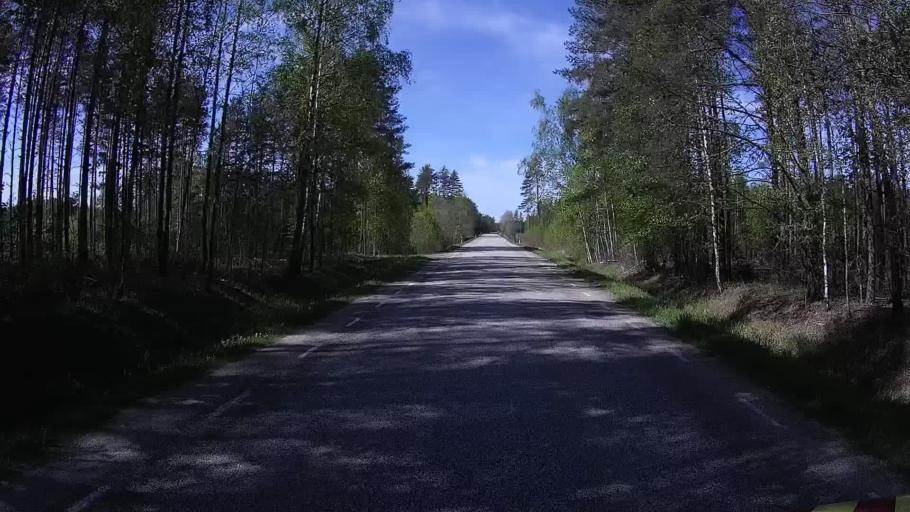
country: EE
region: Polvamaa
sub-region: Raepina vald
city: Rapina
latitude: 57.9742
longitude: 27.5647
